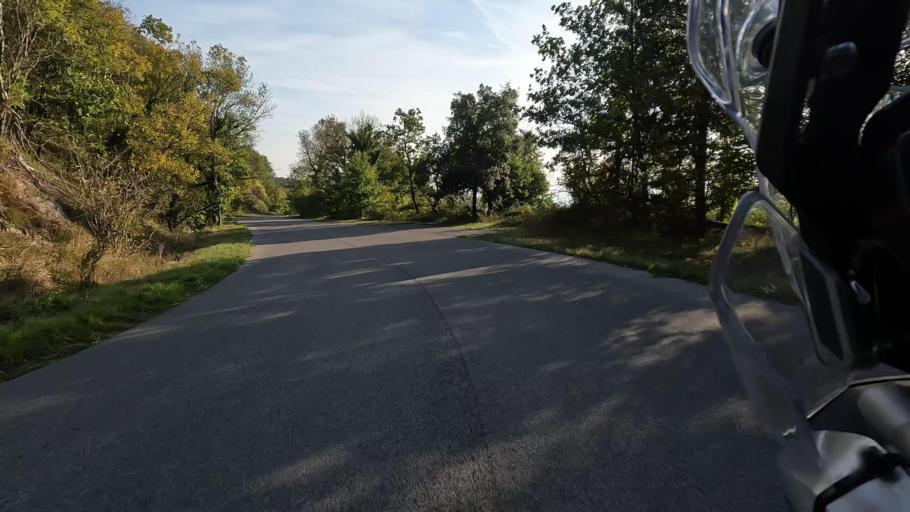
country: IT
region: Liguria
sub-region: Provincia di Savona
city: San Giovanni
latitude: 44.4158
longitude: 8.5286
